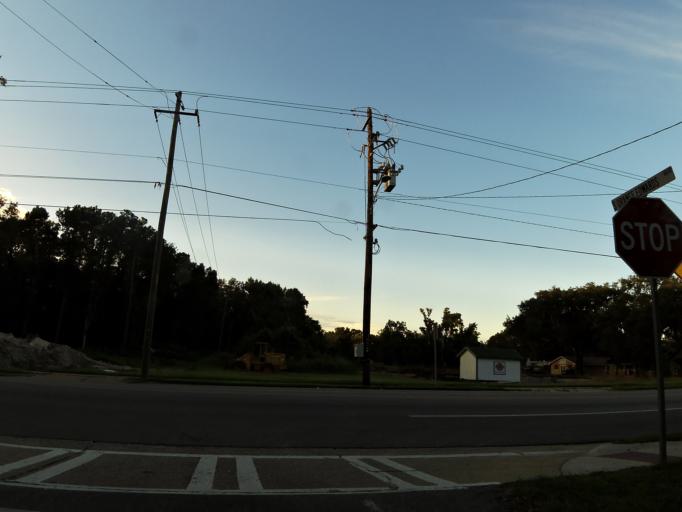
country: US
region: Georgia
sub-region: Camden County
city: Kingsland
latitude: 30.7997
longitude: -81.6917
